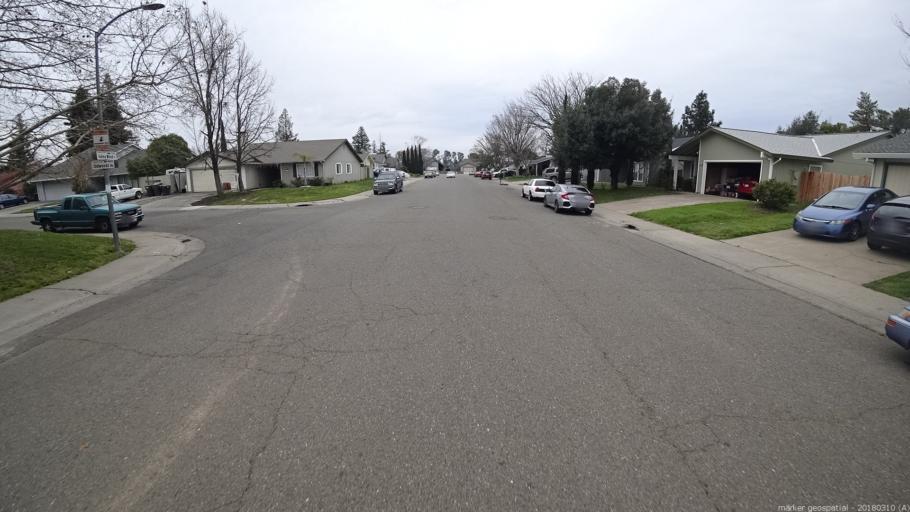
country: US
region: California
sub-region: Sacramento County
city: Florin
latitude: 38.4763
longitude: -121.3862
